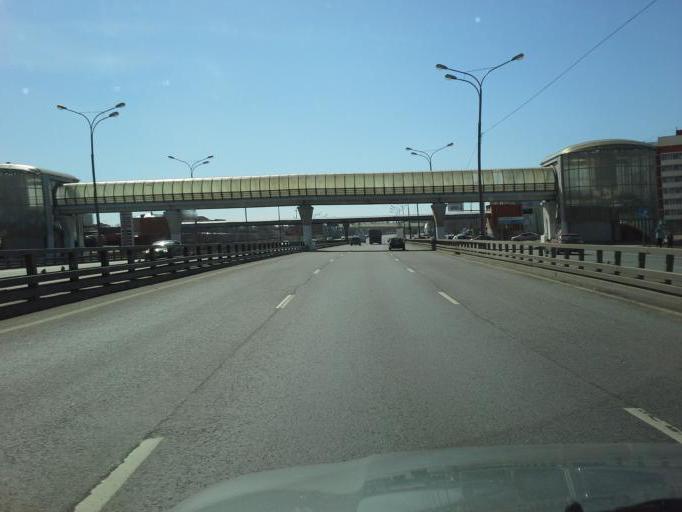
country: RU
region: Moskovskaya
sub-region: Leninskiy Rayon
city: Vnukovo
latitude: 55.6151
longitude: 37.2647
